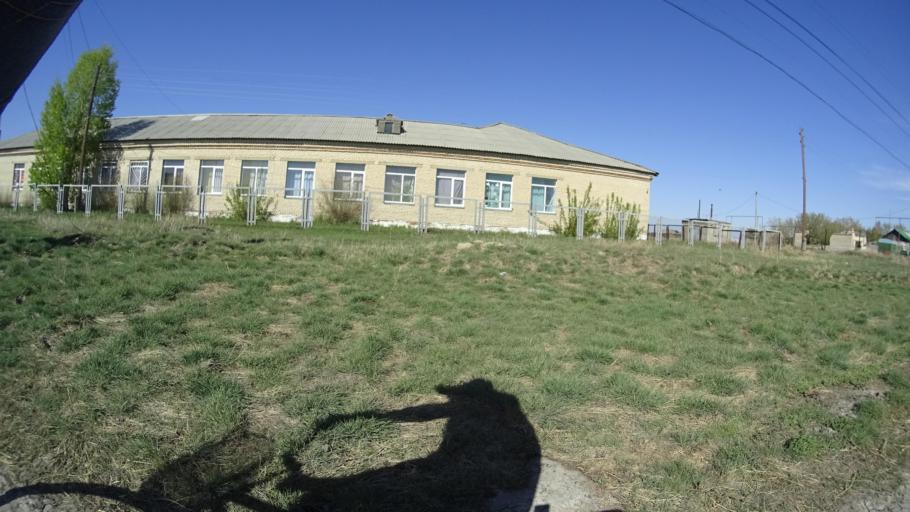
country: RU
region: Chelyabinsk
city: Chesma
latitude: 53.7968
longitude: 61.0332
